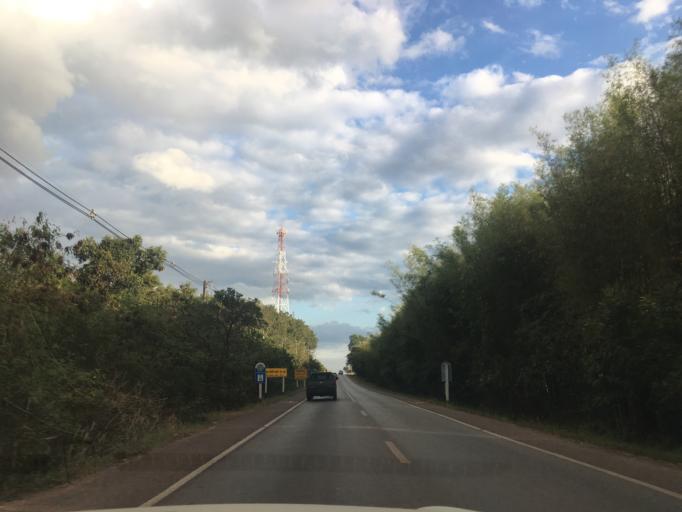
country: TH
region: Chanthaburi
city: Na Yai Am
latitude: 12.7365
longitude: 101.7426
